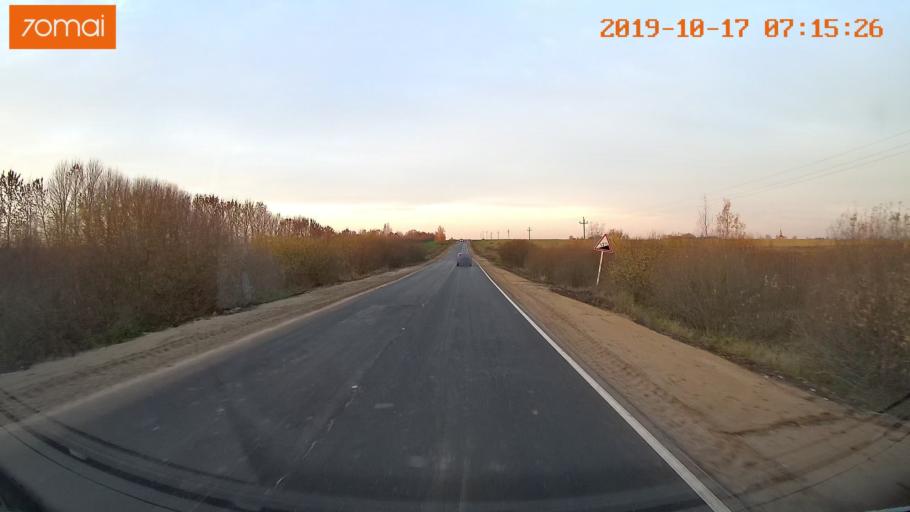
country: RU
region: Vladimir
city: Suzdal'
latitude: 56.3807
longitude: 40.2678
